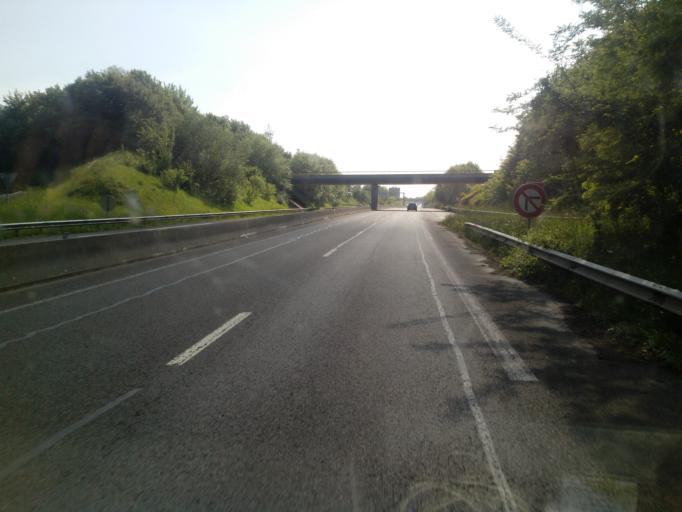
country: FR
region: Picardie
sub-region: Departement de la Somme
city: Abbeville
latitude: 50.0564
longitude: 1.7825
